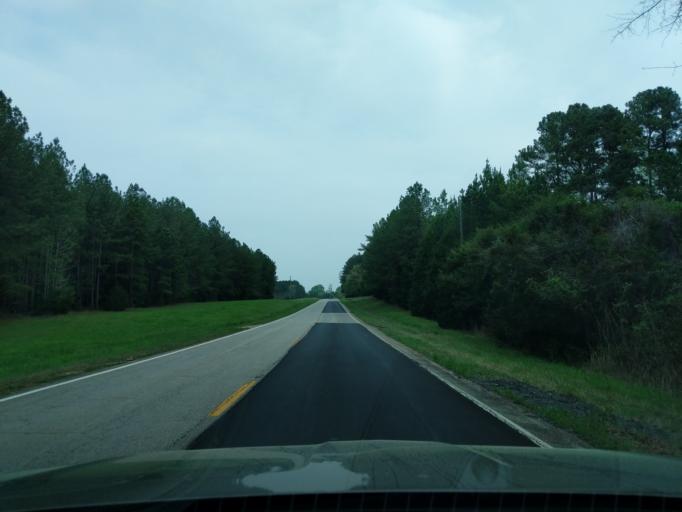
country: US
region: Georgia
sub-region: Lincoln County
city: Lincolnton
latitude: 33.7976
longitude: -82.3868
